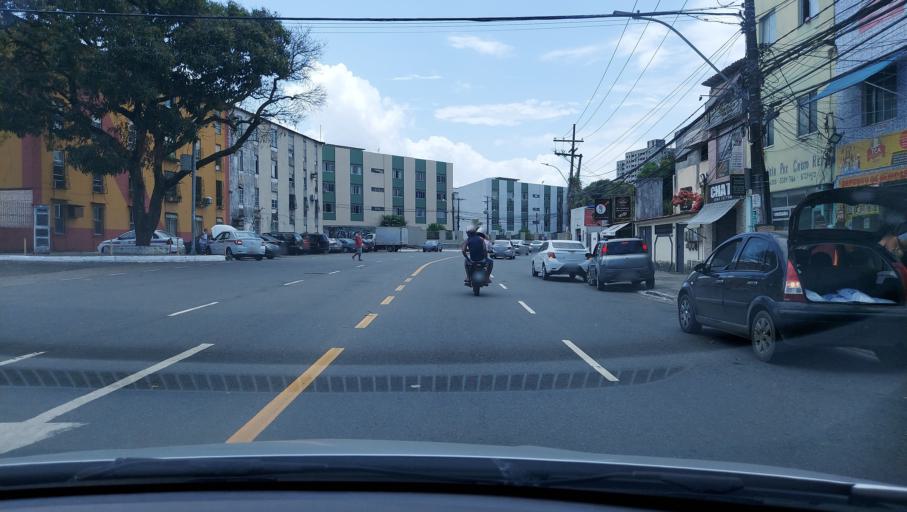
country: BR
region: Bahia
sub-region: Salvador
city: Salvador
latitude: -12.9617
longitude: -38.4710
